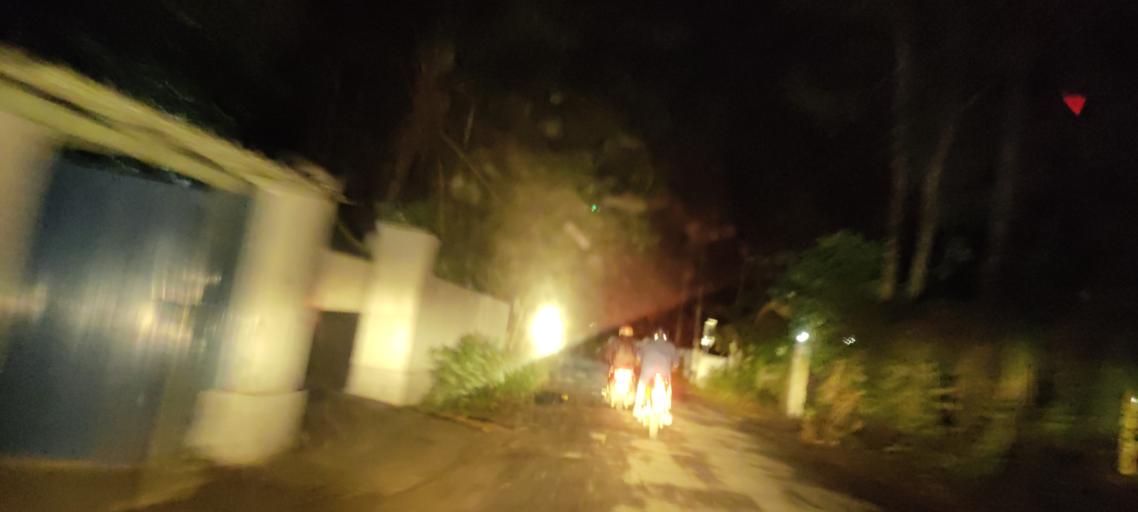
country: IN
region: Kerala
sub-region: Alappuzha
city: Vayalar
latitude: 9.7236
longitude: 76.3198
